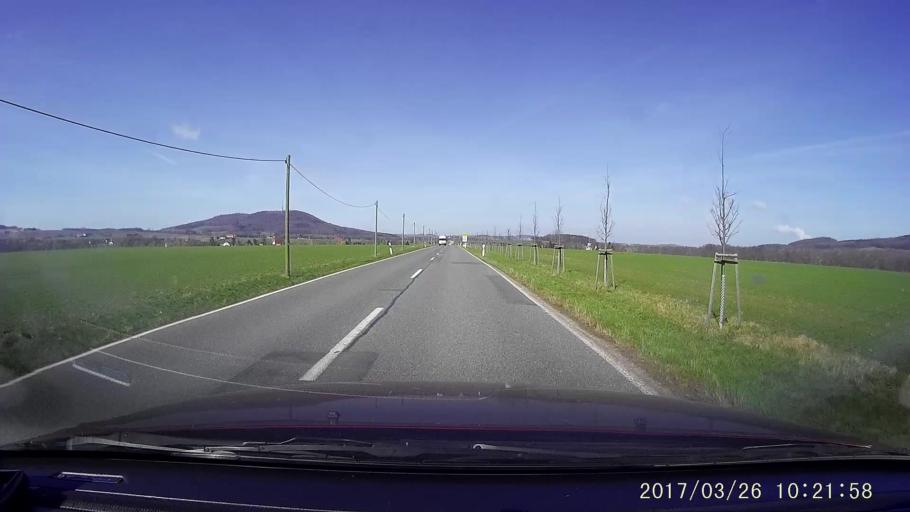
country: DE
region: Saxony
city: Sohland am Rotstein
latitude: 51.0883
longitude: 14.7523
